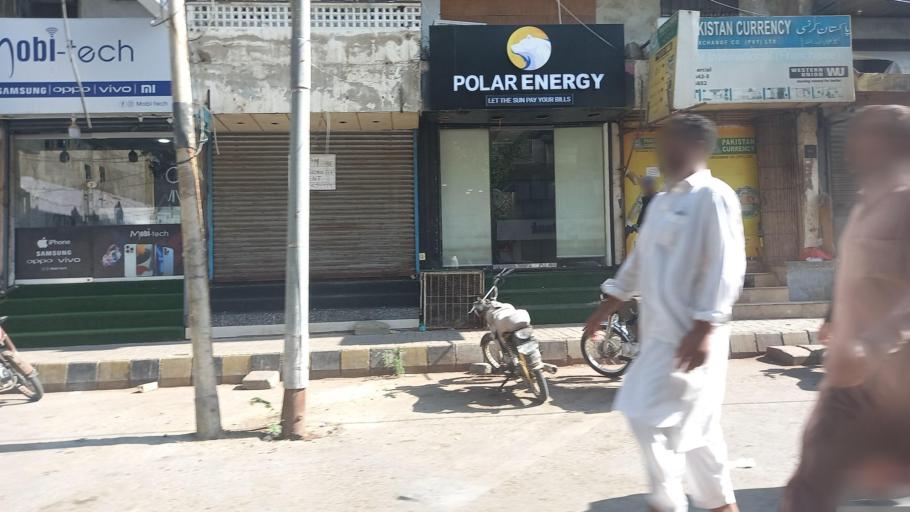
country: PK
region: Sindh
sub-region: Karachi District
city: Karachi
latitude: 24.7981
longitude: 67.0453
